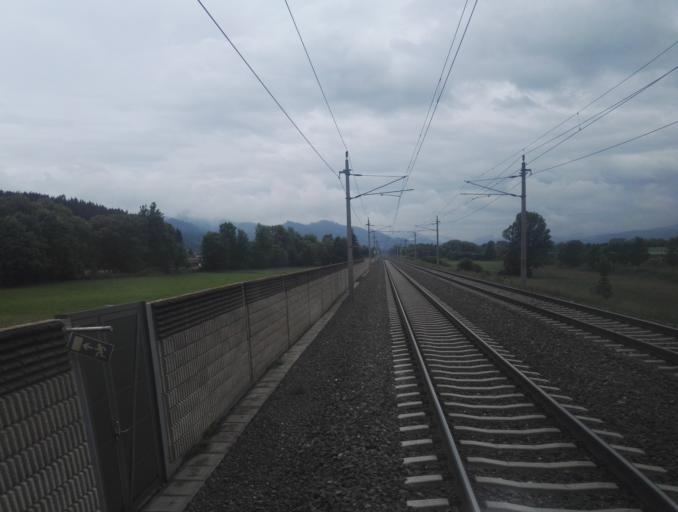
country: AT
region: Styria
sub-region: Politischer Bezirk Bruck-Muerzzuschlag
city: Allerheiligen im Muerztal
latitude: 47.4904
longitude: 15.4177
